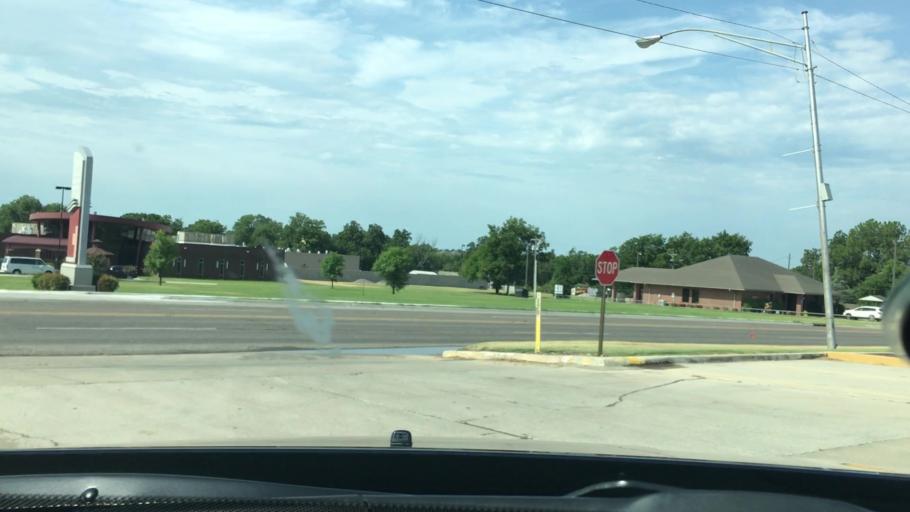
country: US
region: Oklahoma
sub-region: Murray County
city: Sulphur
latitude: 34.5066
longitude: -96.9956
